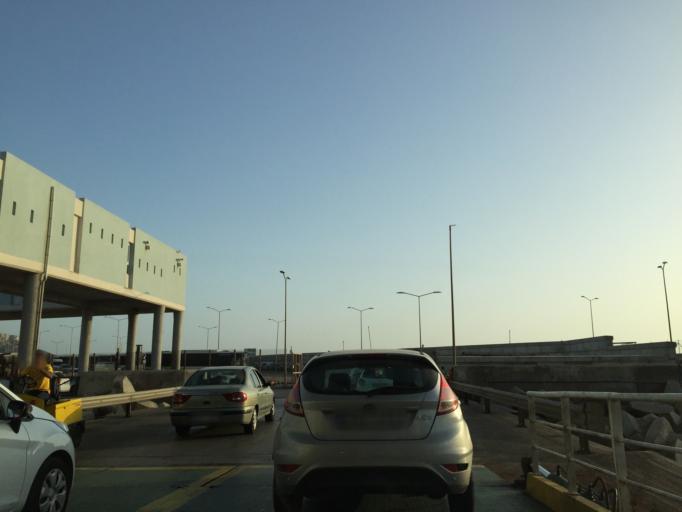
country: MT
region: Il-Mellieha
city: Mellieha
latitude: 35.9892
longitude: 14.3291
